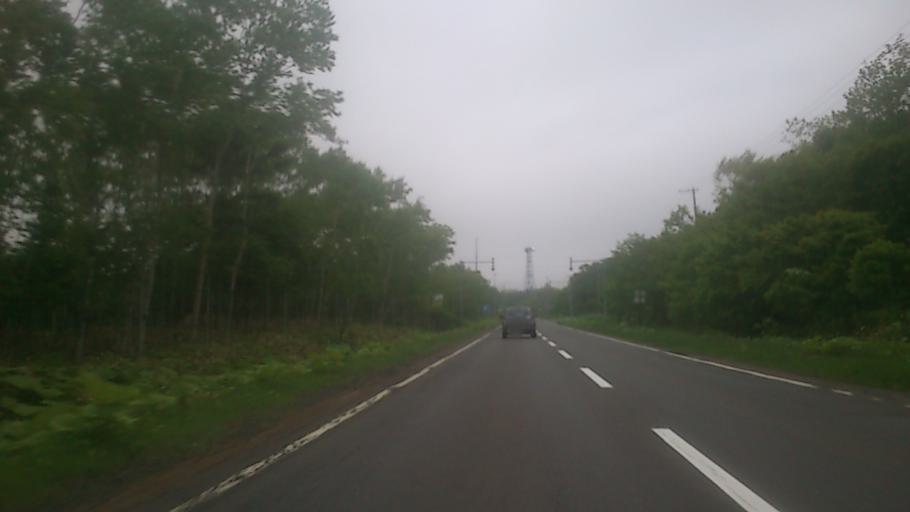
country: JP
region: Hokkaido
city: Kushiro
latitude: 42.9809
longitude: 144.5918
